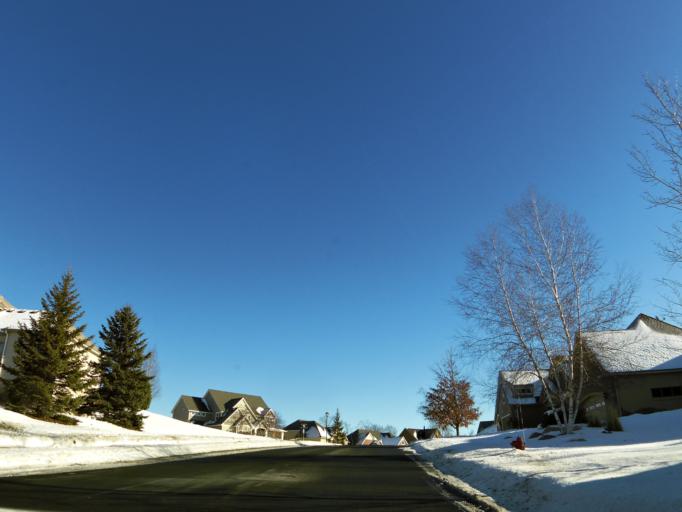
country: US
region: Minnesota
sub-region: Scott County
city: Prior Lake
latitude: 44.7417
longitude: -93.4551
